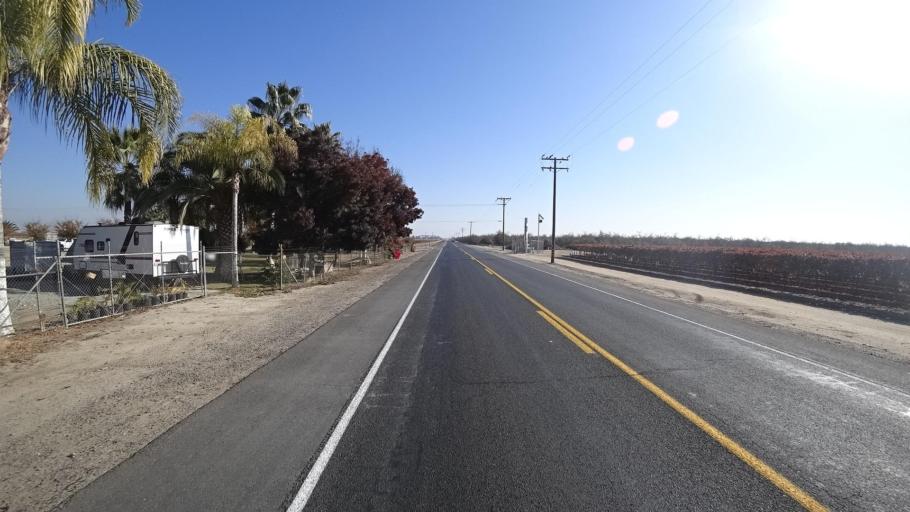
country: US
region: California
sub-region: Kern County
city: McFarland
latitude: 35.7178
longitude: -119.2595
